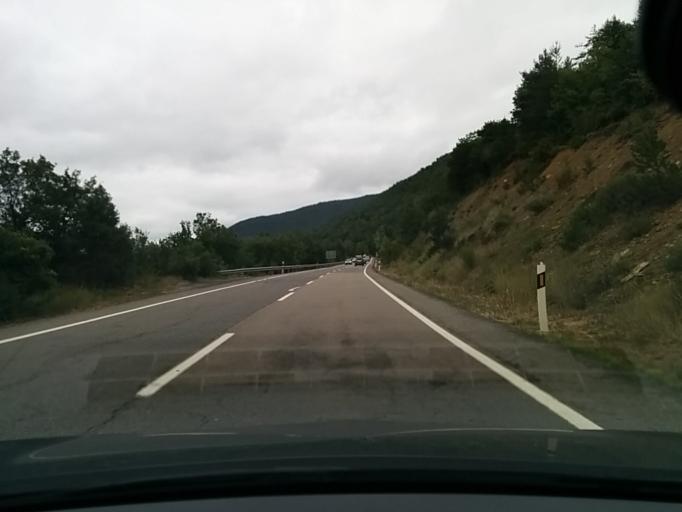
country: ES
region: Aragon
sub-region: Provincia de Huesca
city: Sabinanigo
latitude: 42.4737
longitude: -0.3831
